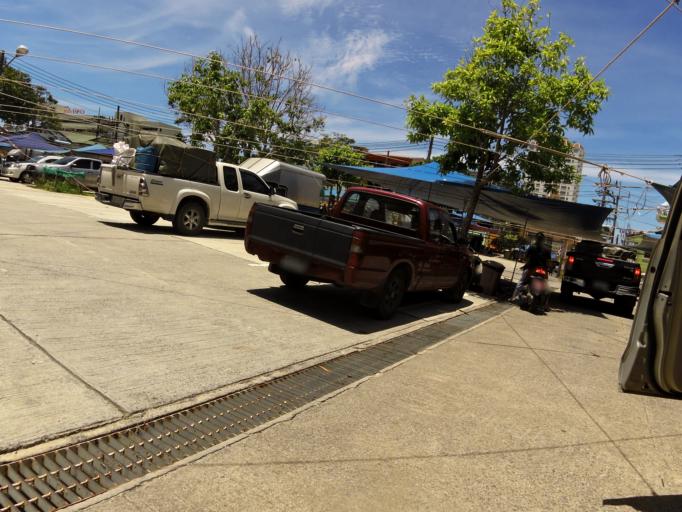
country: TH
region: Phuket
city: Ban Karon
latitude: 7.8482
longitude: 98.2980
